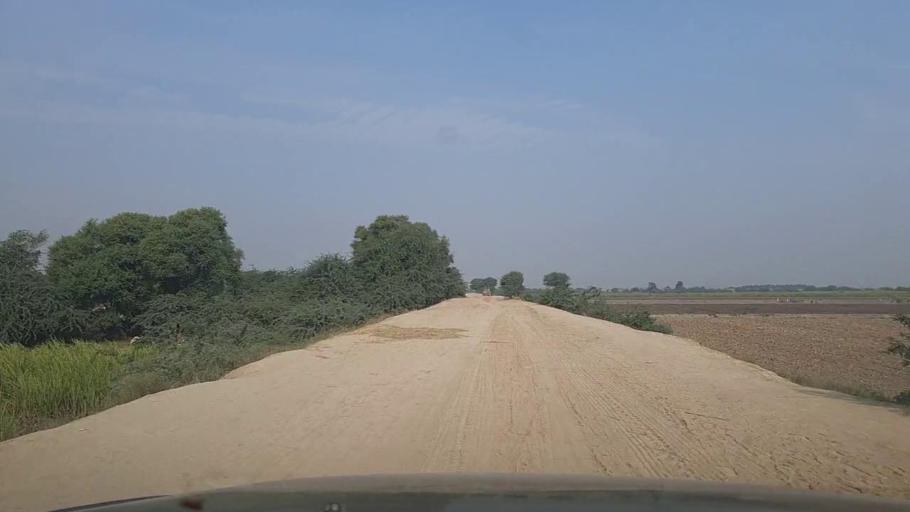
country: PK
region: Sindh
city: Bulri
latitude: 25.0266
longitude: 68.2813
